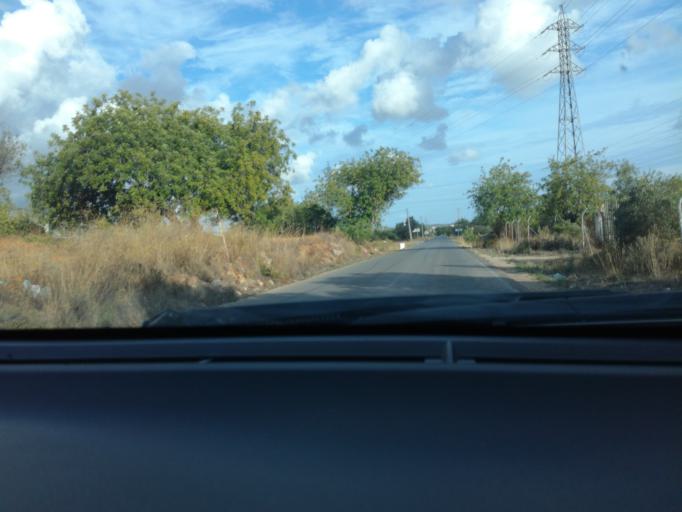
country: PT
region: Faro
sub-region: Olhao
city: Olhao
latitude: 37.0821
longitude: -7.8549
